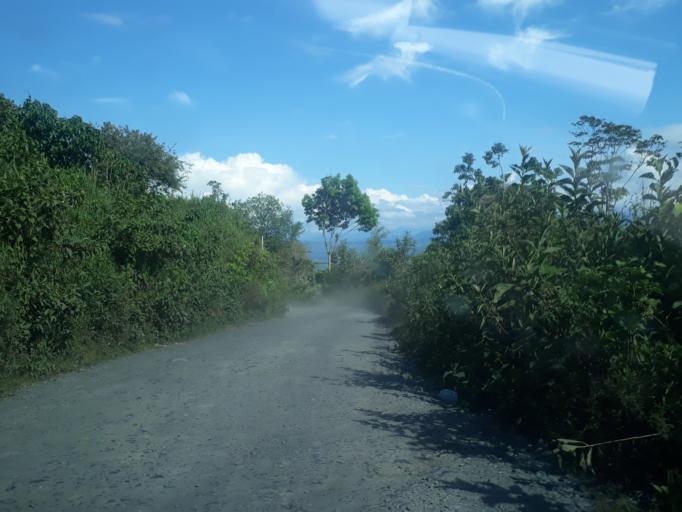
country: CO
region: Santander
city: Velez
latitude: 6.0221
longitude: -73.6610
